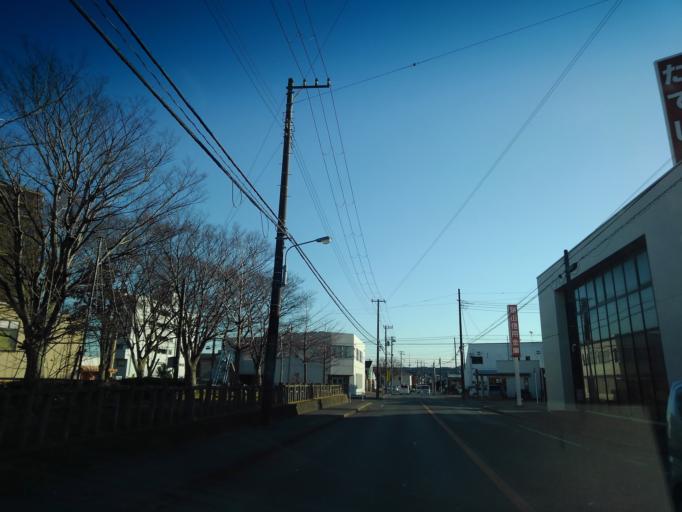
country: JP
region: Chiba
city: Kimitsu
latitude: 35.3304
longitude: 139.8996
